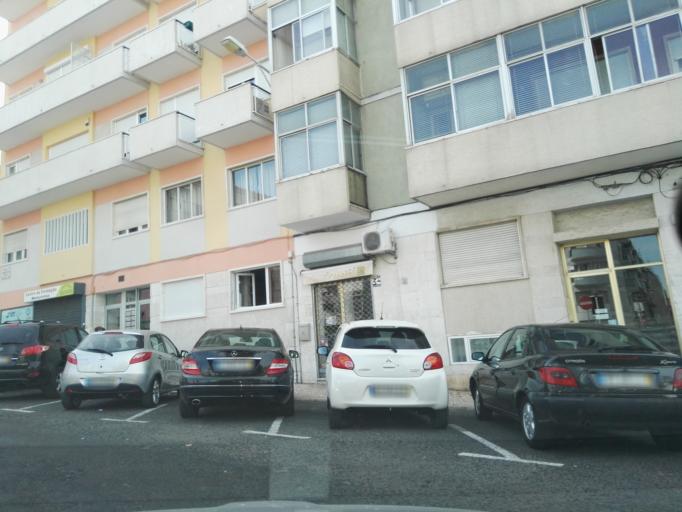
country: PT
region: Lisbon
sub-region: Lisbon
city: Lisbon
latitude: 38.7201
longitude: -9.1668
